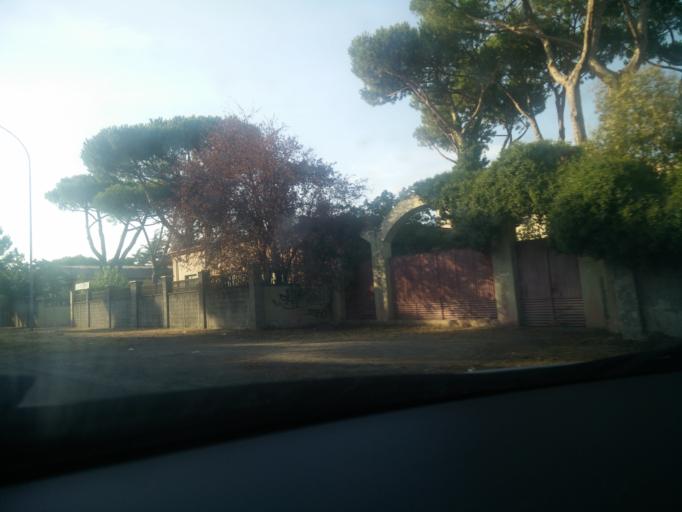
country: IT
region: Tuscany
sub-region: Provincia di Massa-Carrara
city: Massa
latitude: 44.0291
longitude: 10.1035
